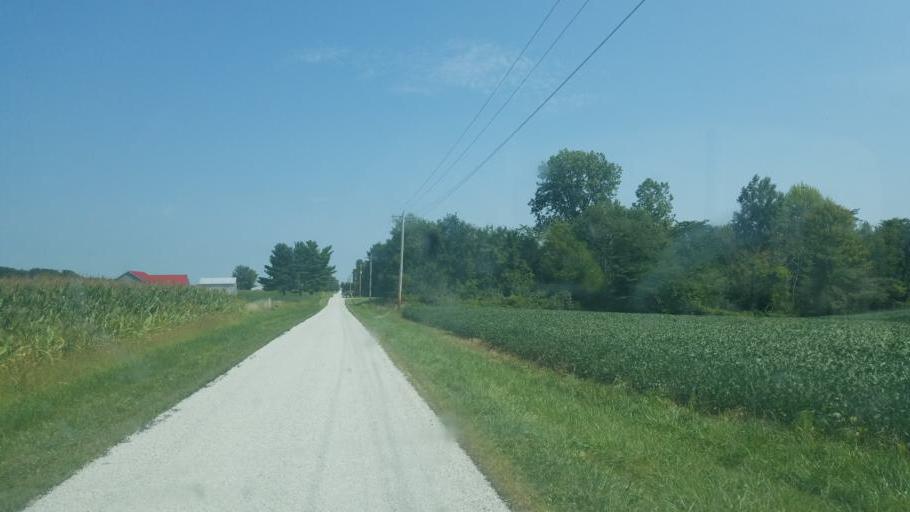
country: US
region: Ohio
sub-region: Crawford County
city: Bucyrus
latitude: 40.9359
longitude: -83.0525
